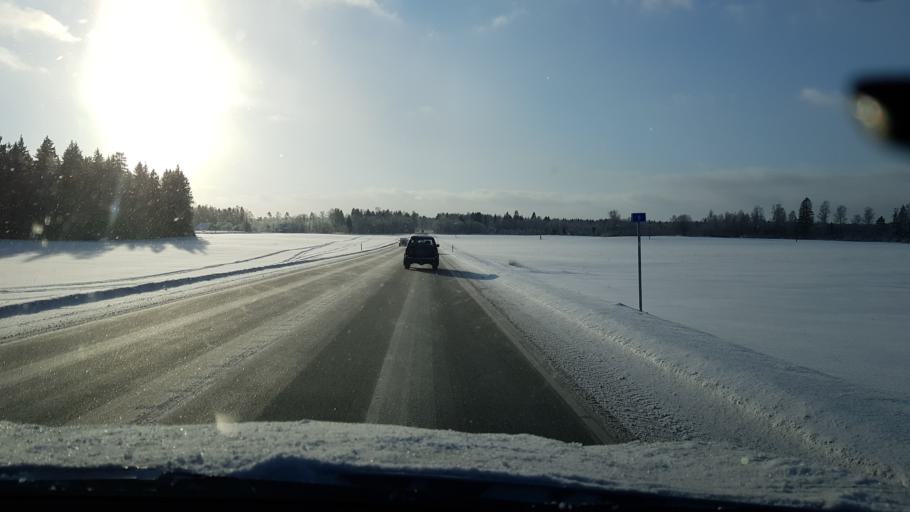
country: EE
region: Harju
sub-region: Keila linn
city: Keila
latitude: 59.2175
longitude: 24.4357
